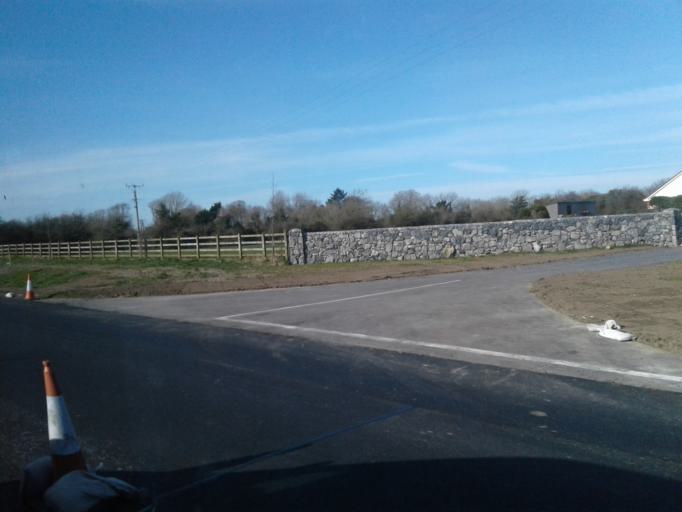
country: IE
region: Connaught
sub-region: County Galway
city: Gort
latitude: 53.1792
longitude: -8.8404
